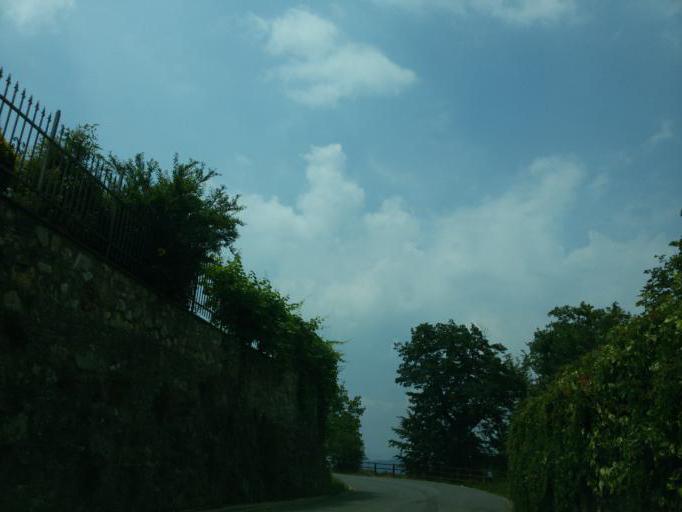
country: IT
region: Liguria
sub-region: Provincia di Genova
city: Piccarello
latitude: 44.4378
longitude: 9.0116
